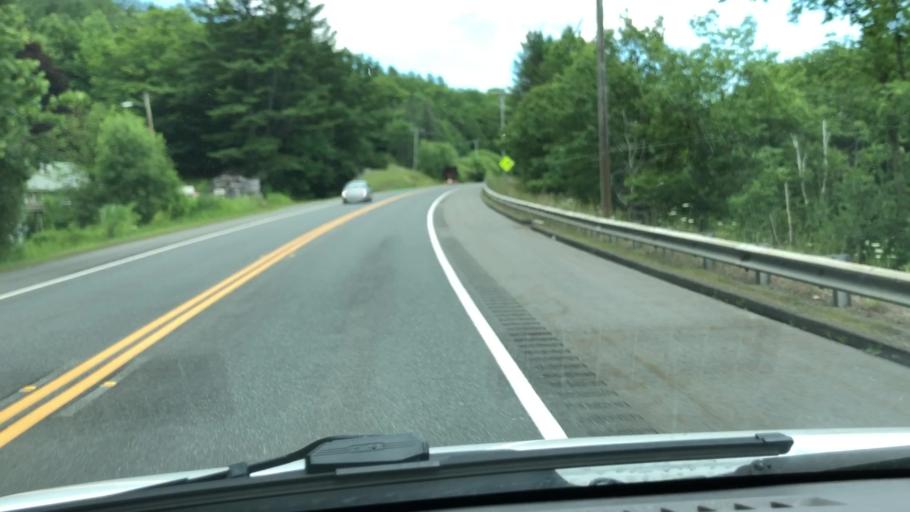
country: US
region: Massachusetts
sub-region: Hampshire County
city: Chesterfield
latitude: 42.4904
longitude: -72.9539
